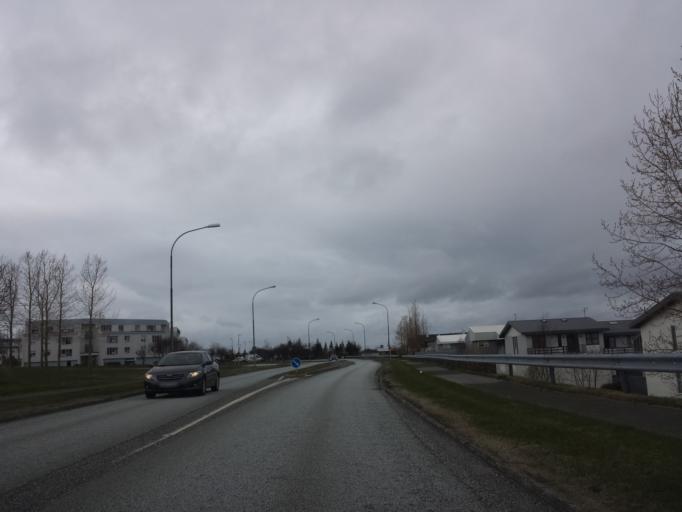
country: IS
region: Capital Region
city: Gardabaer
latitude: 64.0917
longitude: -21.9121
